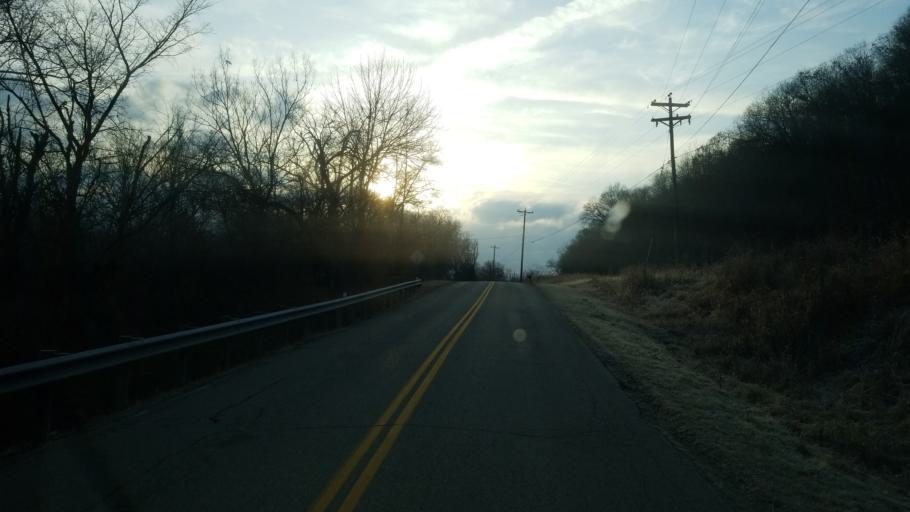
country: US
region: Ohio
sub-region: Ross County
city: Chillicothe
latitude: 39.2823
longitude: -82.9359
